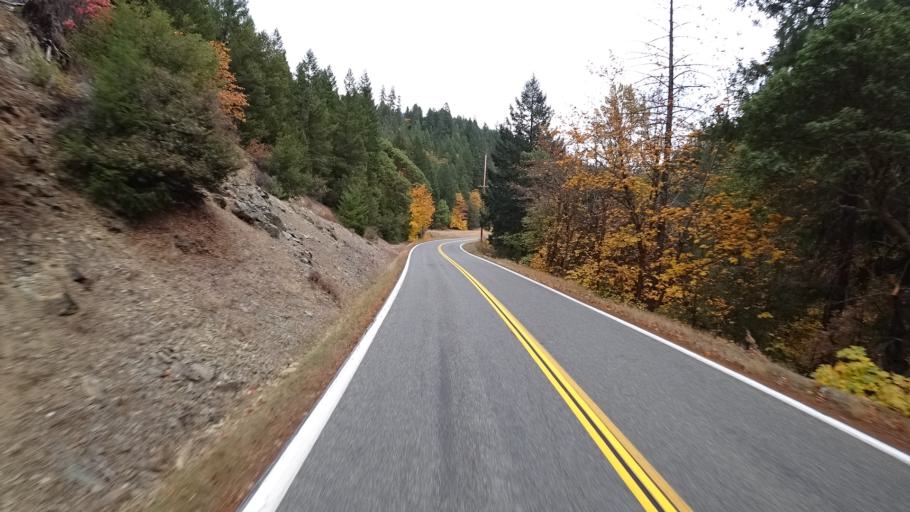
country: US
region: California
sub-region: Siskiyou County
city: Happy Camp
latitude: 41.9089
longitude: -123.4464
